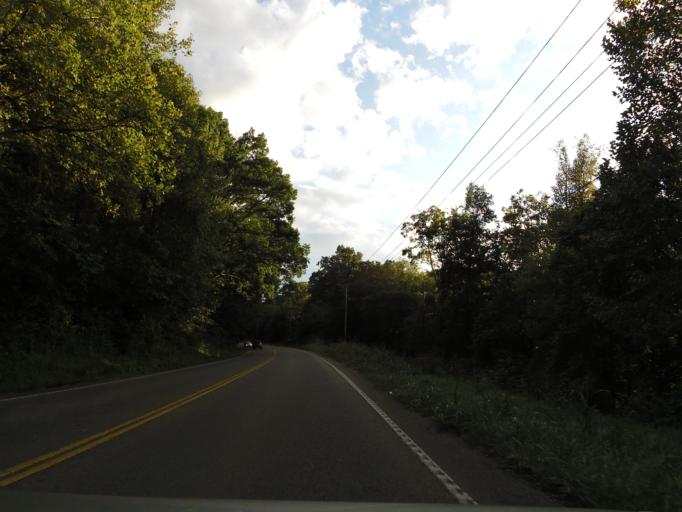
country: US
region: Tennessee
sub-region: Jefferson County
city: Jefferson City
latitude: 36.1509
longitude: -83.5273
